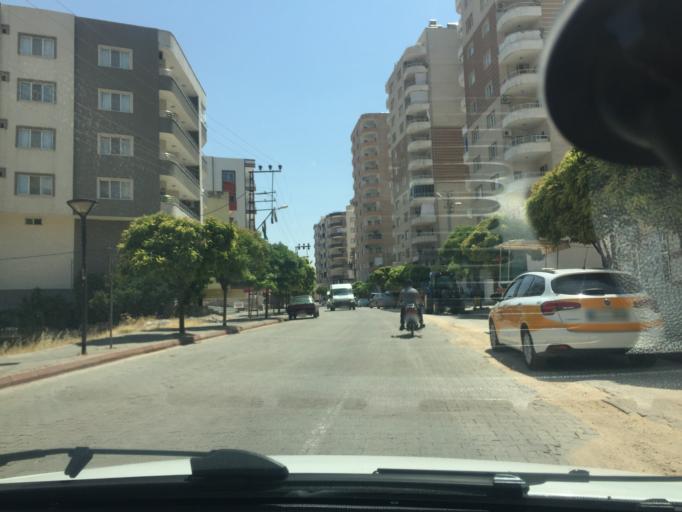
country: TR
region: Mardin
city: Midyat
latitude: 37.4310
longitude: 41.3369
